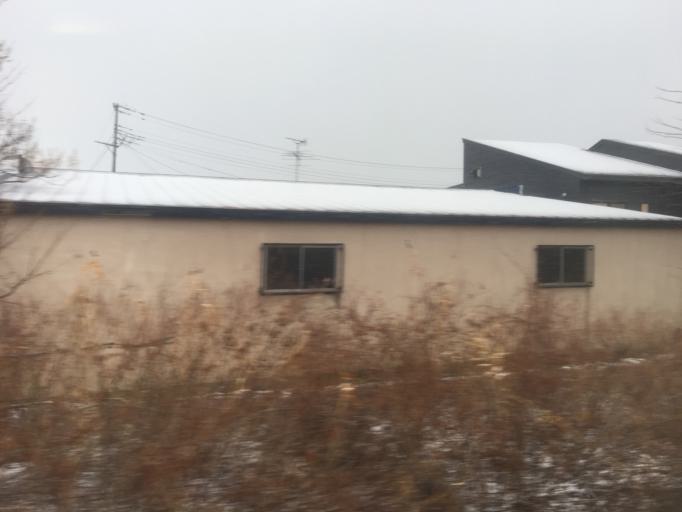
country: JP
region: Aomori
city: Aomori Shi
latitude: 40.8330
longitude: 140.7083
